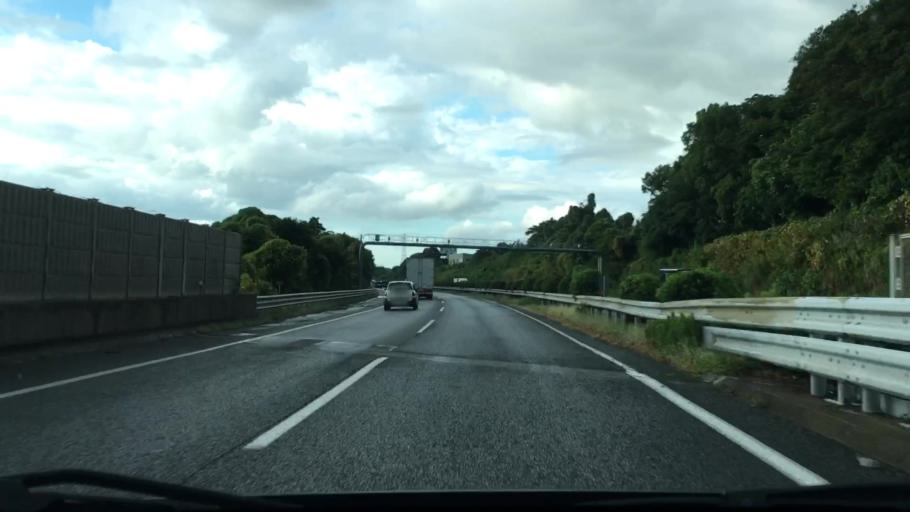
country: JP
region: Fukuoka
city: Koga
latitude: 33.6973
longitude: 130.4854
